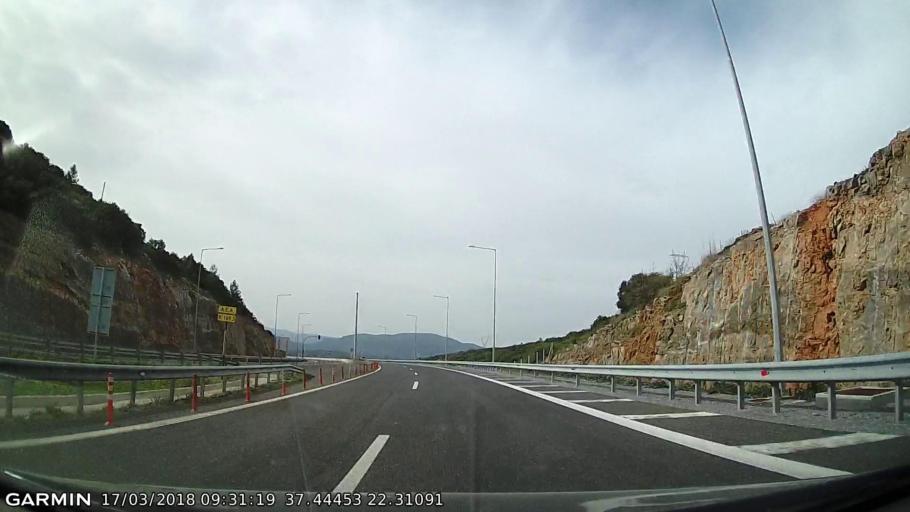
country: GR
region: Peloponnese
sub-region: Nomos Arkadias
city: Tripoli
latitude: 37.4434
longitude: 22.3109
